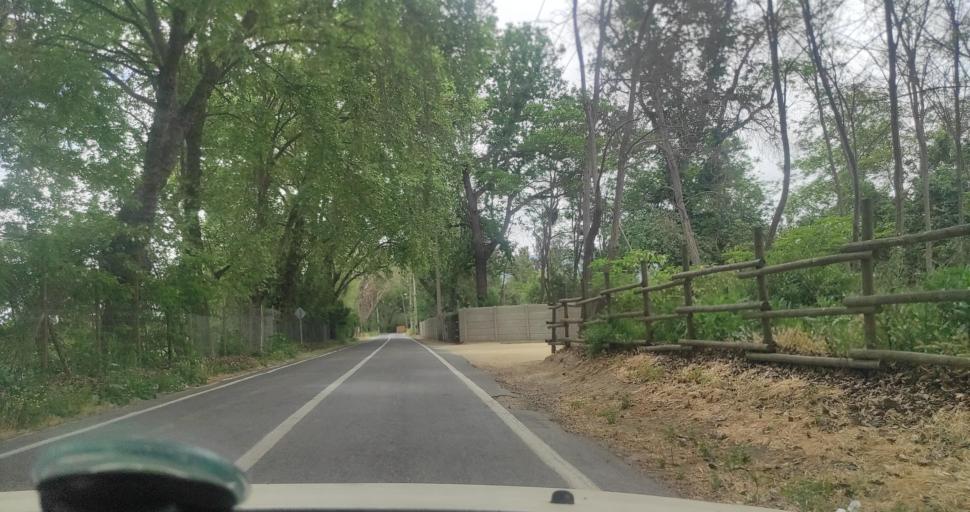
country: CL
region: Valparaiso
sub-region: Provincia de Marga Marga
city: Limache
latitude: -33.0233
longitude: -71.2414
